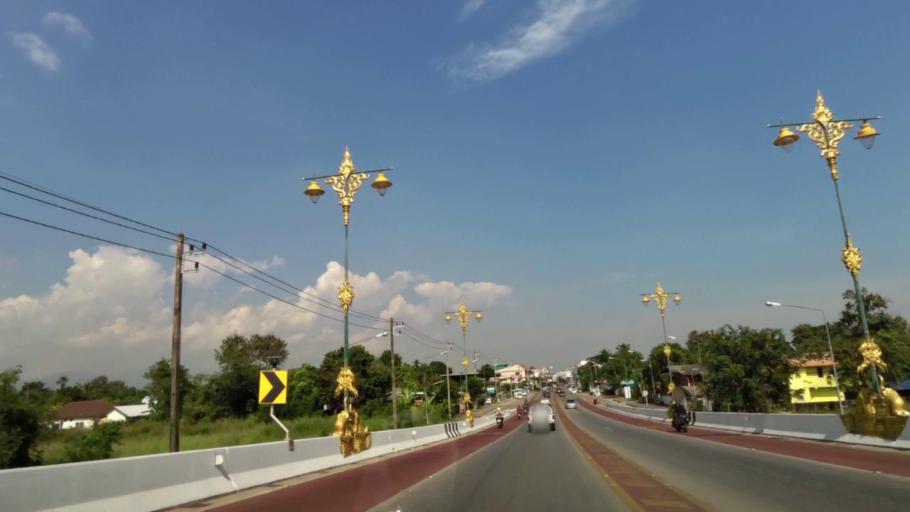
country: TH
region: Chiang Rai
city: Chiang Rai
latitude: 19.9201
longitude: 99.8332
